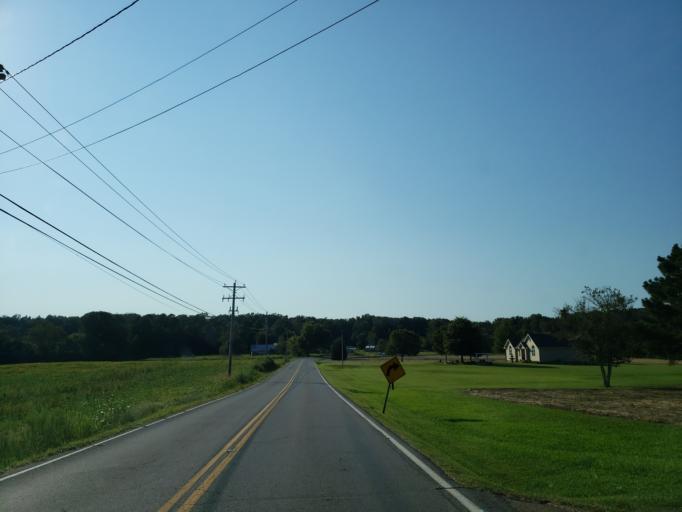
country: US
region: Tennessee
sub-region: Bradley County
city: Wildwood Lake
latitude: 35.0346
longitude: -84.7384
